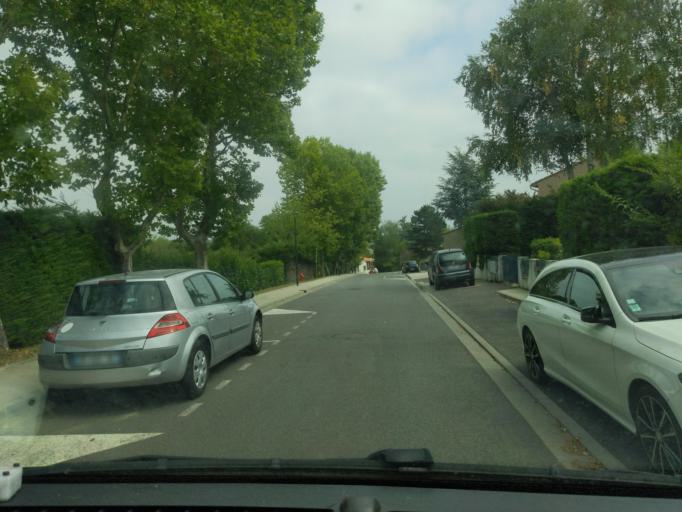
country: FR
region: Midi-Pyrenees
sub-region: Departement de la Haute-Garonne
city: Labege
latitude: 43.5335
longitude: 1.5423
